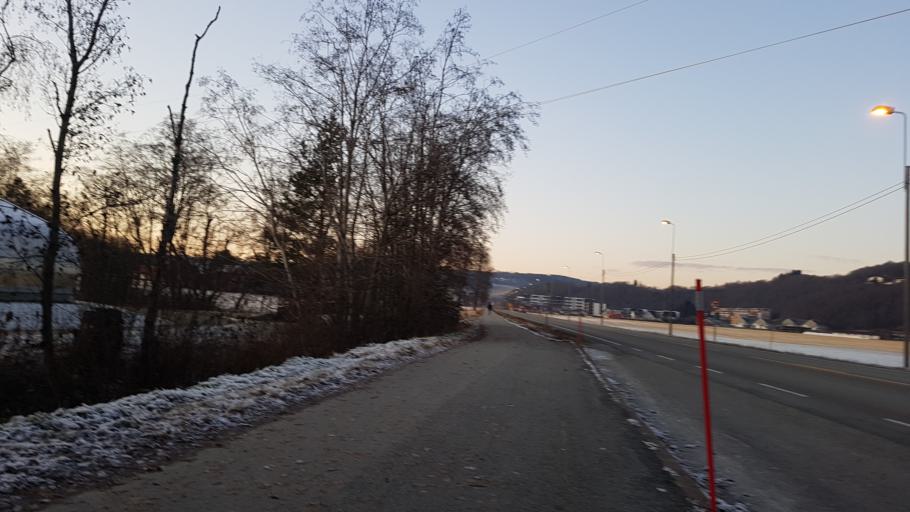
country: NO
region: Sor-Trondelag
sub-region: Melhus
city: Melhus
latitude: 63.2786
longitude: 10.2898
